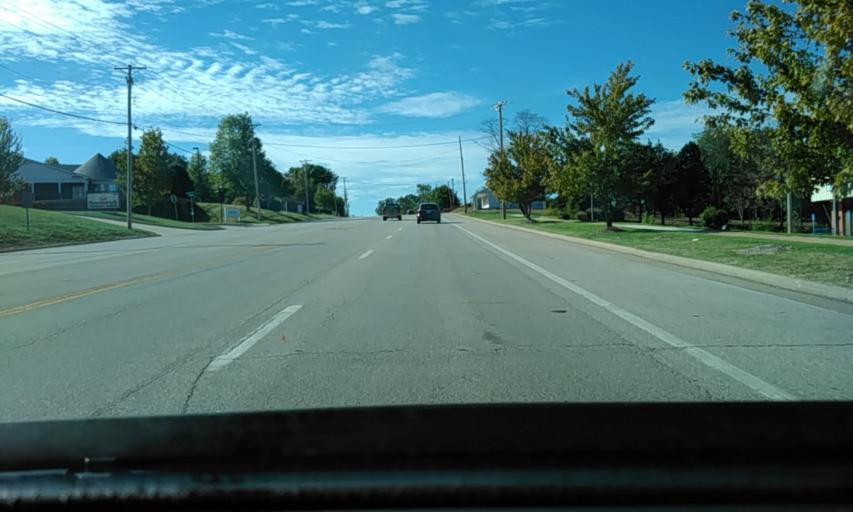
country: US
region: Missouri
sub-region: Saint Louis County
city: Mehlville
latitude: 38.4922
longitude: -90.3463
